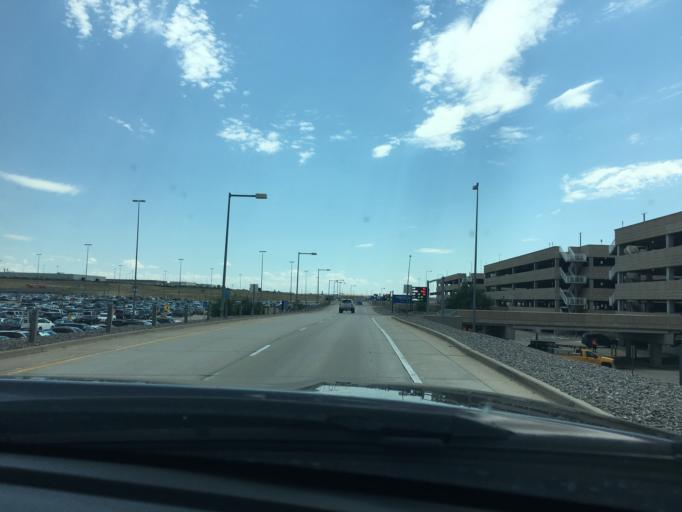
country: US
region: Colorado
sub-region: Weld County
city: Lochbuie
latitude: 39.8498
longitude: -104.6699
